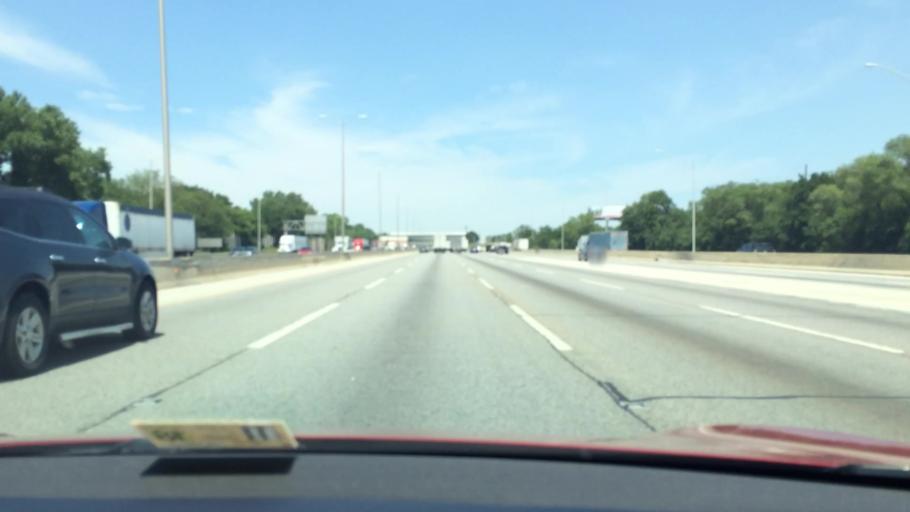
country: US
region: Illinois
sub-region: Cook County
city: Indian Head Park
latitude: 41.7762
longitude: -87.9076
